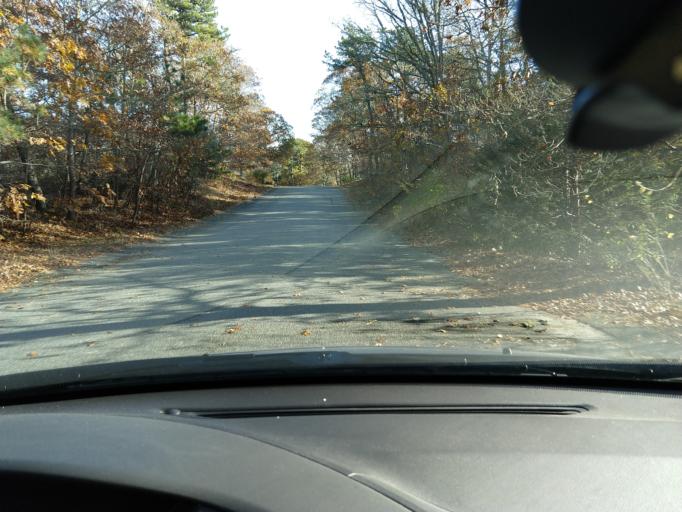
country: US
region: Massachusetts
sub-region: Barnstable County
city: Orleans
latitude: 41.7800
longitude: -70.0315
